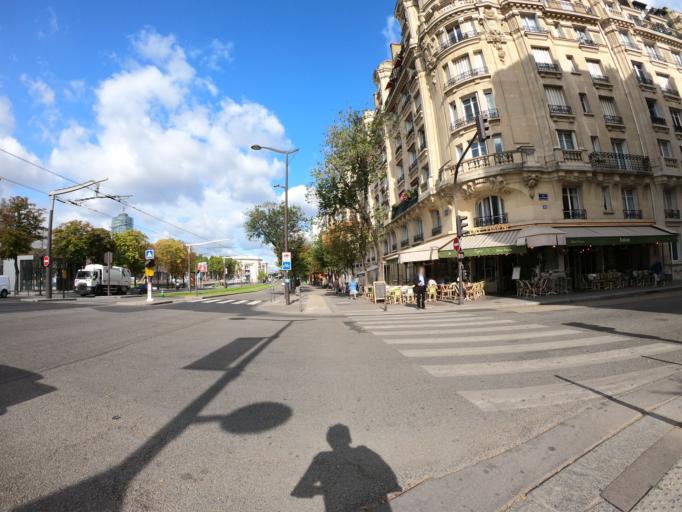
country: FR
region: Ile-de-France
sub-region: Departement des Hauts-de-Seine
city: Vanves
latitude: 48.8335
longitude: 2.2868
